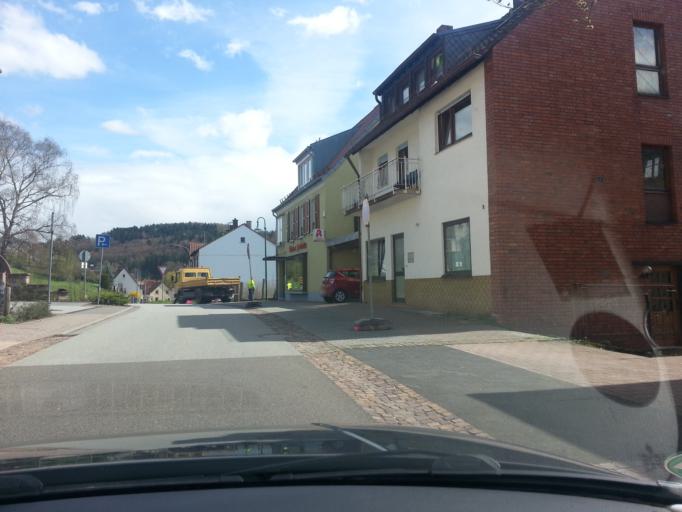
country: DE
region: Rheinland-Pfalz
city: Thaleischweiler-Froschen
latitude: 49.2625
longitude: 7.5786
